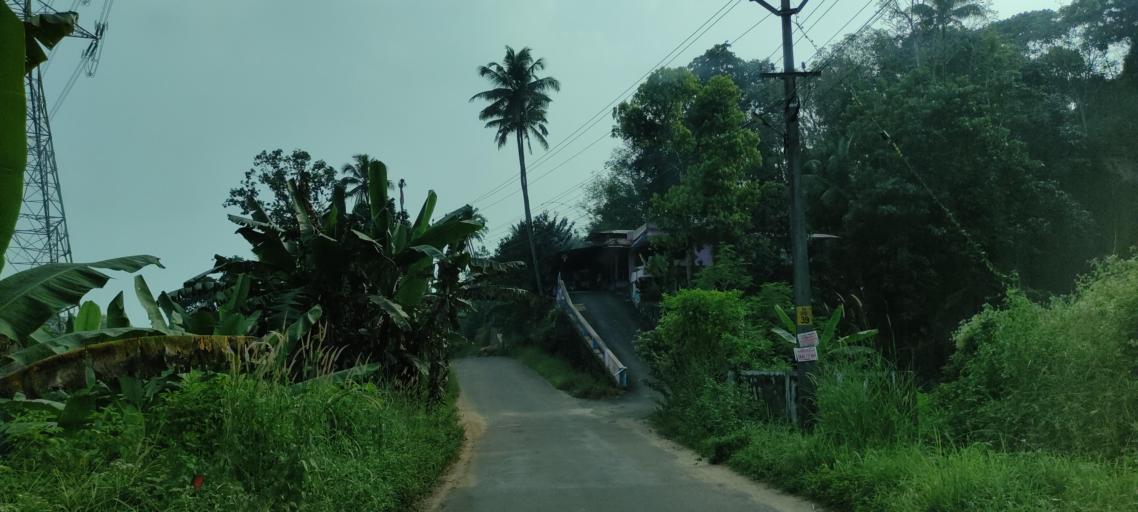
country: IN
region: Kerala
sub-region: Ernakulam
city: Piravam
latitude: 9.8021
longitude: 76.5355
